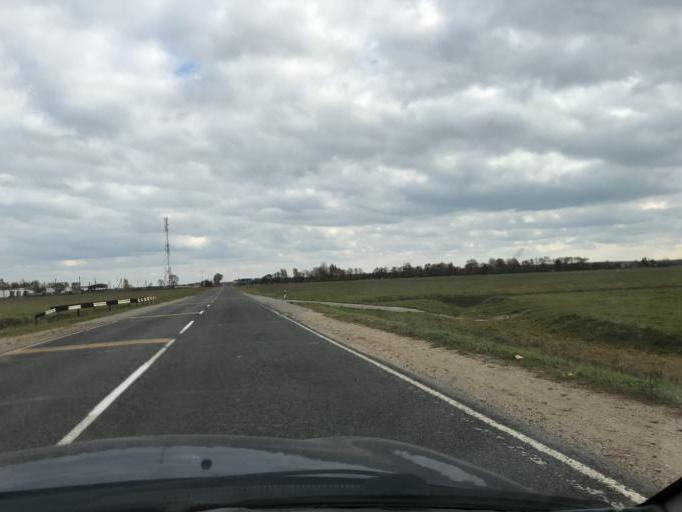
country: BY
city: Berezovka
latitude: 53.7406
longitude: 25.3632
